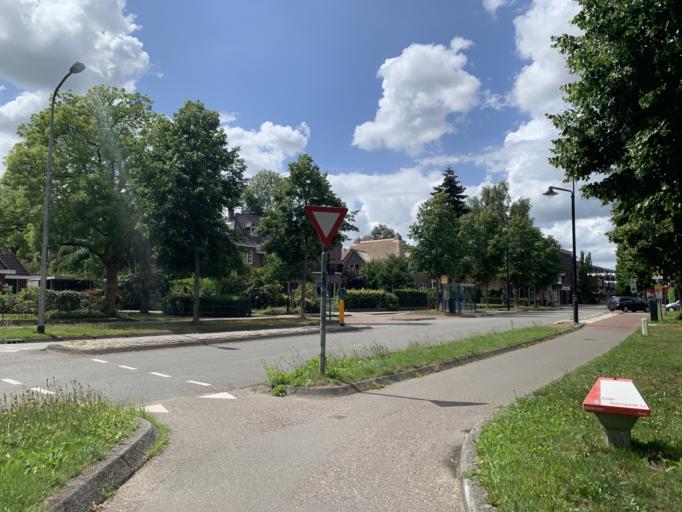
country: NL
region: Groningen
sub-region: Gemeente Haren
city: Haren
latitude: 53.1704
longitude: 6.6067
